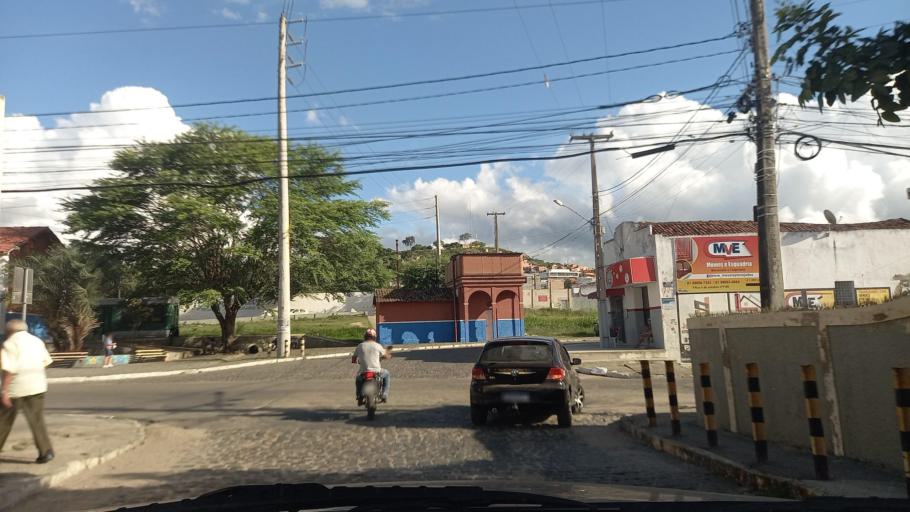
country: BR
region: Pernambuco
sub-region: Gravata
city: Gravata
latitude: -8.2042
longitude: -35.5730
